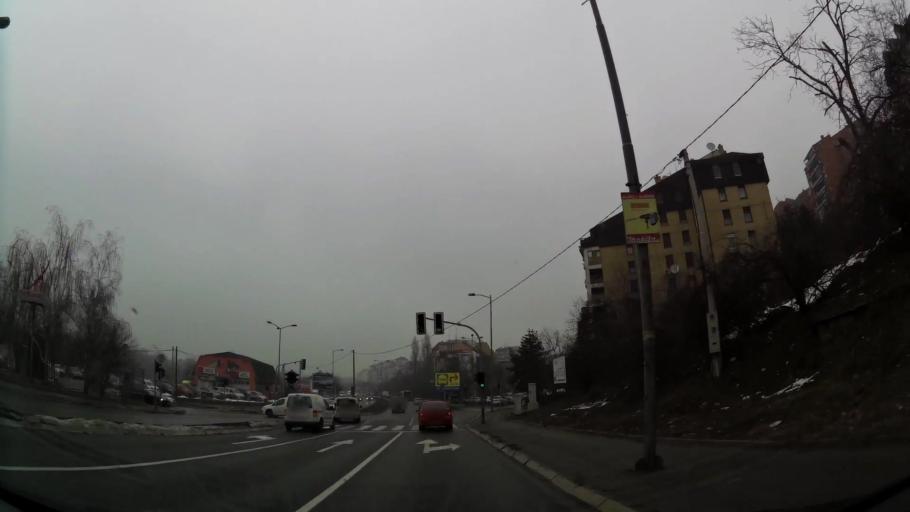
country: RS
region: Central Serbia
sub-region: Belgrade
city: Cukarica
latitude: 44.7722
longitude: 20.4091
